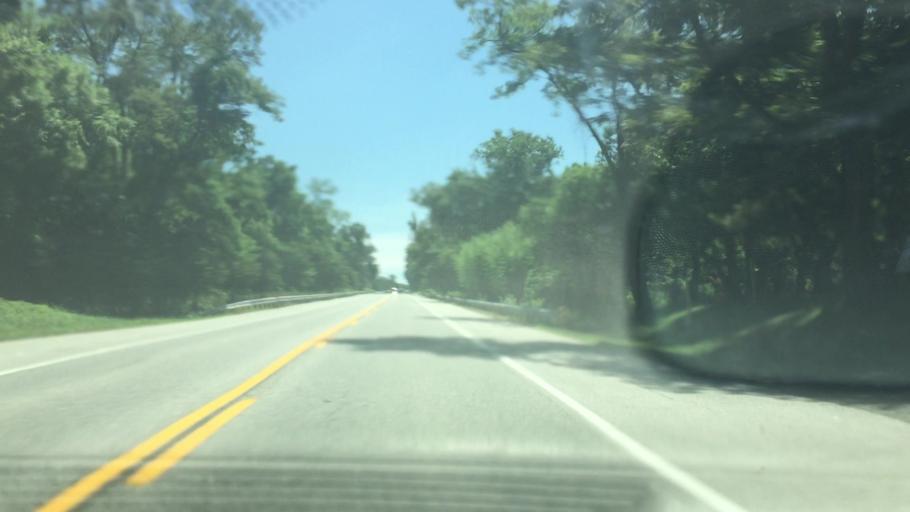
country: US
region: Maryland
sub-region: Cecil County
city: Rising Sun
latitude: 39.6472
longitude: -76.0730
